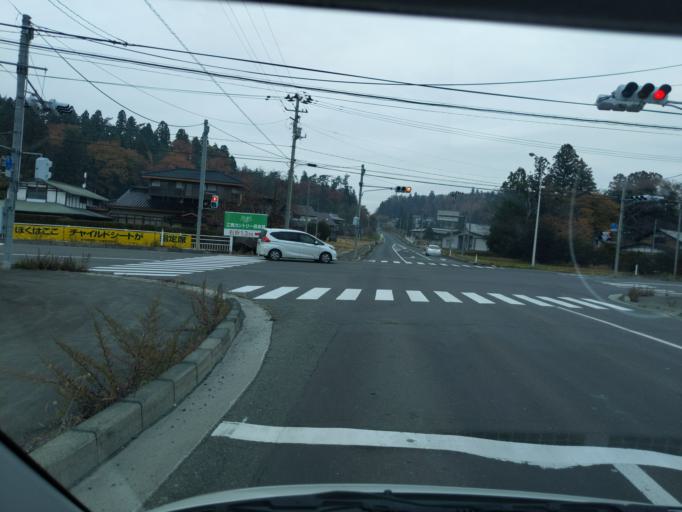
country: JP
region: Iwate
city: Mizusawa
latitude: 39.1605
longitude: 141.2008
